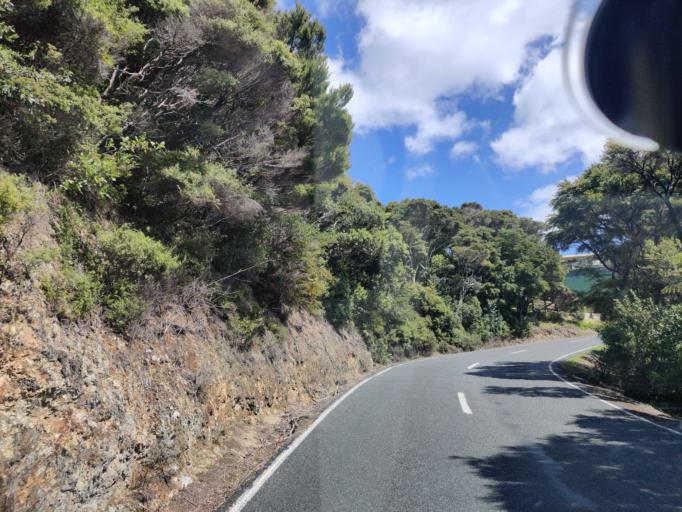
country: NZ
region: Northland
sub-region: Far North District
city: Paihia
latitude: -35.2600
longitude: 174.2451
